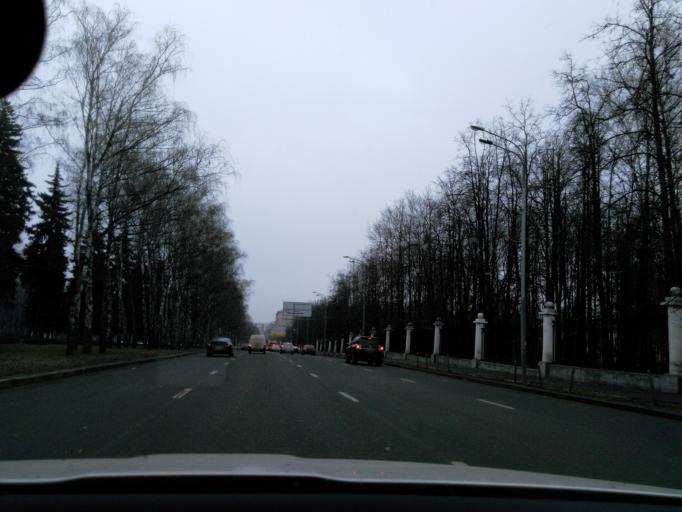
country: RU
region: Moscow
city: Vorob'yovo
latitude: 55.7026
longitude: 37.5420
